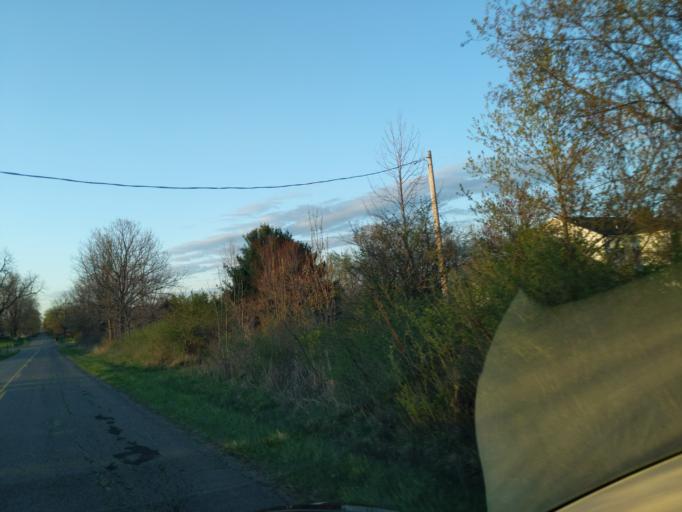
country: US
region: Michigan
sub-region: Ingham County
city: Mason
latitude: 42.5228
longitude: -84.4527
